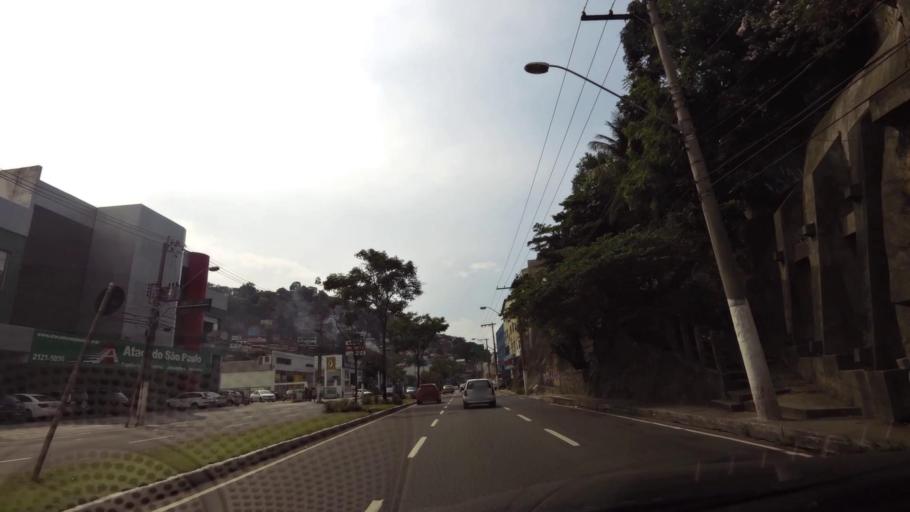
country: BR
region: Espirito Santo
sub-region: Vila Velha
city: Vila Velha
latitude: -20.3102
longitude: -40.3104
